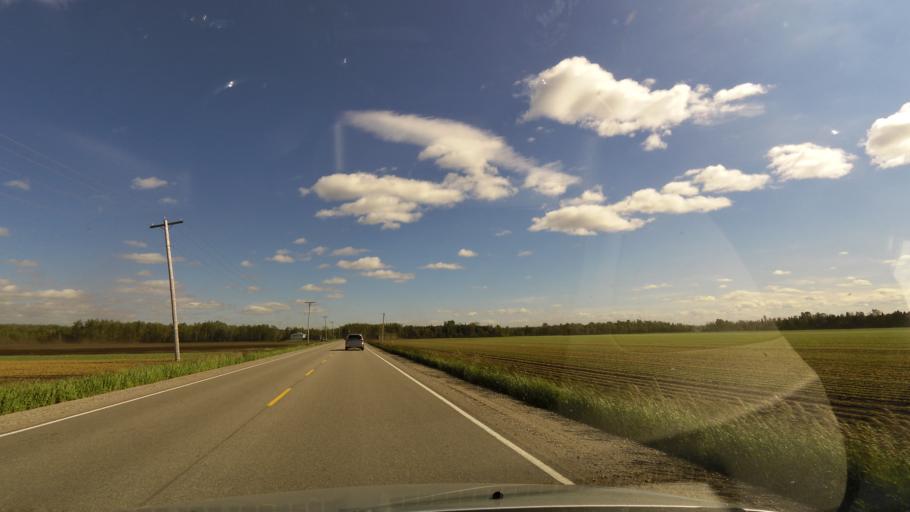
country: CA
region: Ontario
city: Innisfil
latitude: 44.2178
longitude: -79.6310
